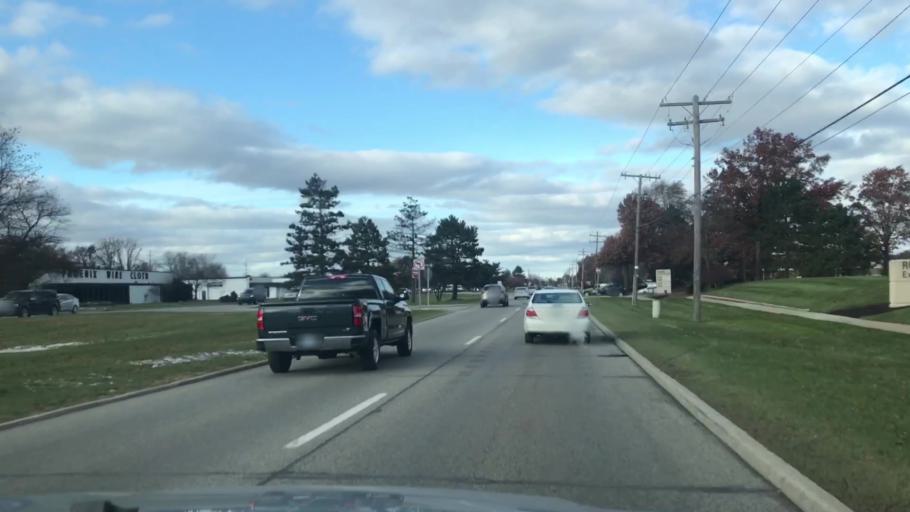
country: US
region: Michigan
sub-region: Oakland County
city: Clawson
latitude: 42.5376
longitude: -83.1200
